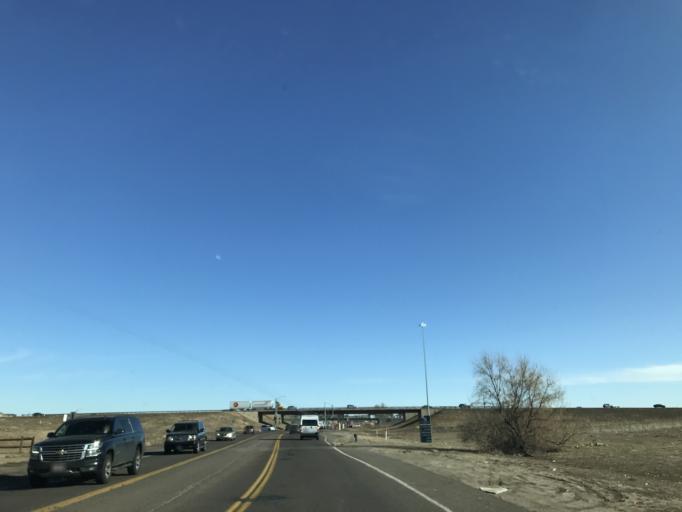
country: US
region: Colorado
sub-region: Adams County
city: Aurora
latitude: 39.7983
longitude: -104.7904
